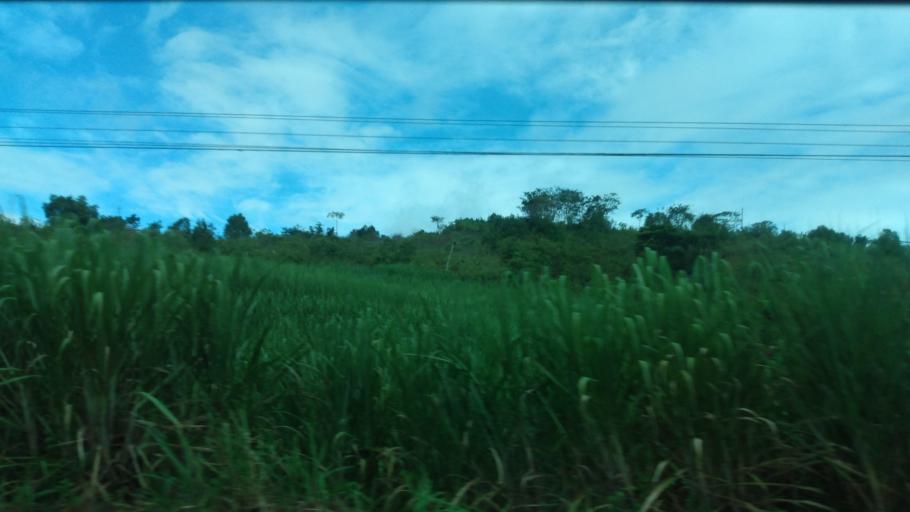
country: BR
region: Pernambuco
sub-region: Catende
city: Catende
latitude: -8.7042
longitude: -35.7478
